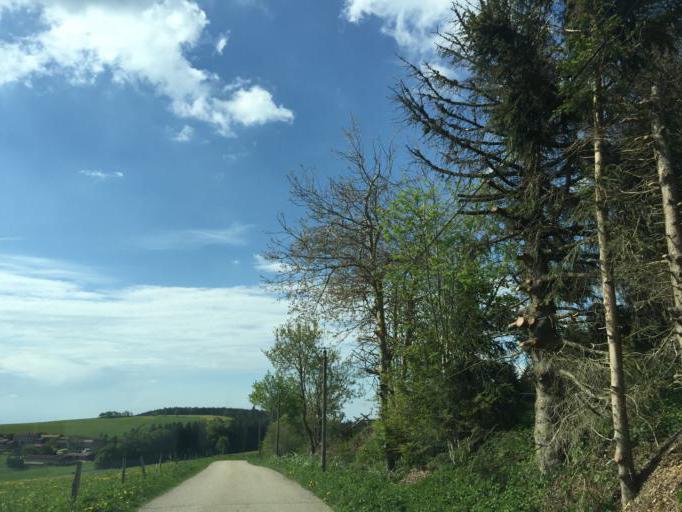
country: FR
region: Rhone-Alpes
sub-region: Departement de la Loire
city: Saint-Sauveur-en-Rue
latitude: 45.3104
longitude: 4.4702
